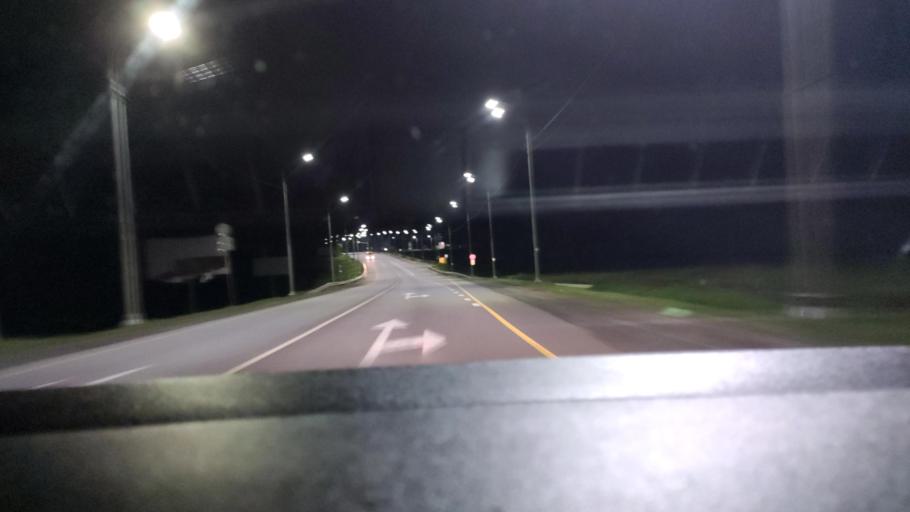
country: RU
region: Voronezj
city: Semiluki
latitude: 51.6516
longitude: 39.0355
